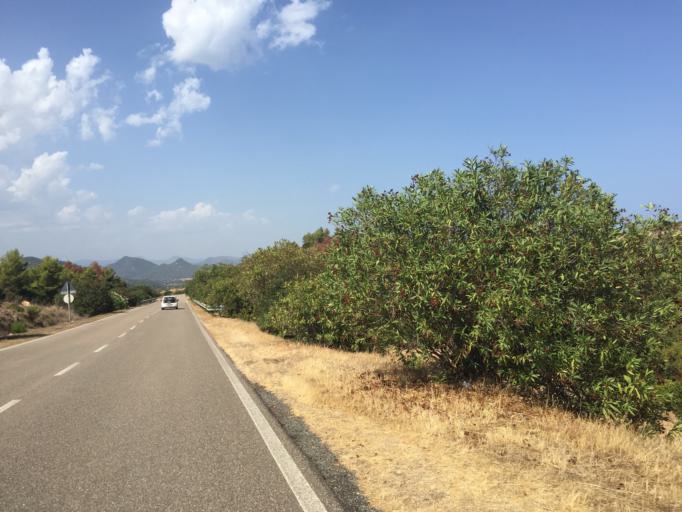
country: IT
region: Sardinia
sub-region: Provincia di Cagliari
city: Villasimius
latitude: 39.1636
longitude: 9.5628
